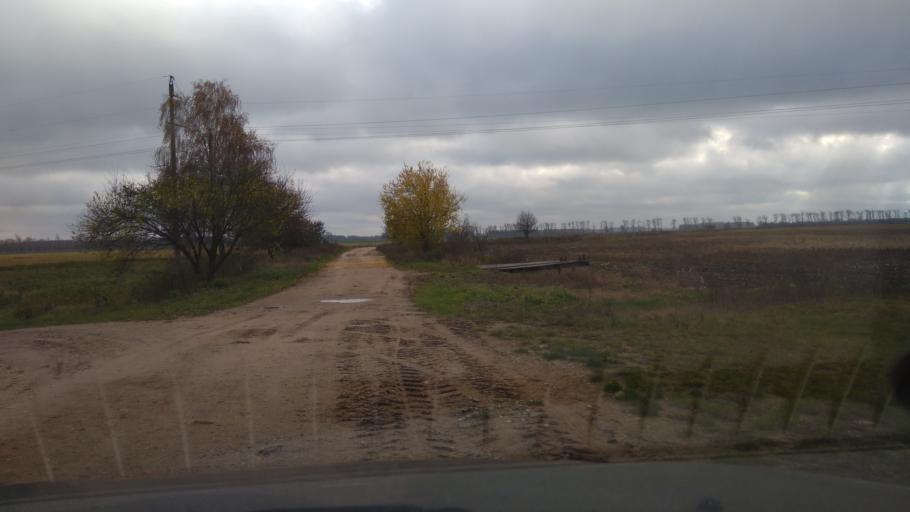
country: BY
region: Minsk
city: Staryya Darohi
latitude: 53.2020
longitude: 28.0455
